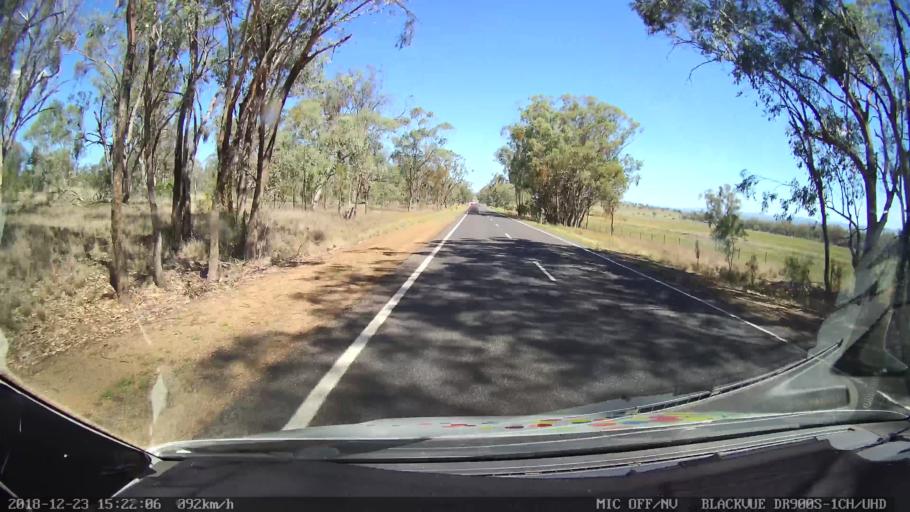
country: AU
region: New South Wales
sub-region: Tamworth Municipality
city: Manilla
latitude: -30.8643
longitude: 150.8018
